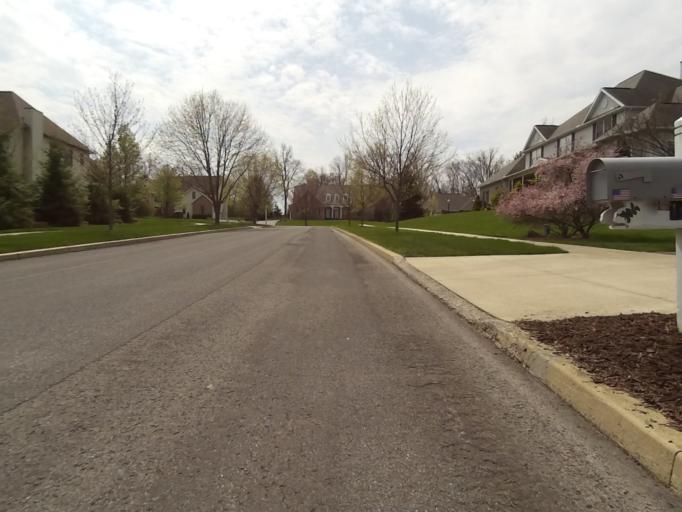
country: US
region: Pennsylvania
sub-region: Centre County
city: State College
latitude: 40.7926
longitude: -77.8880
